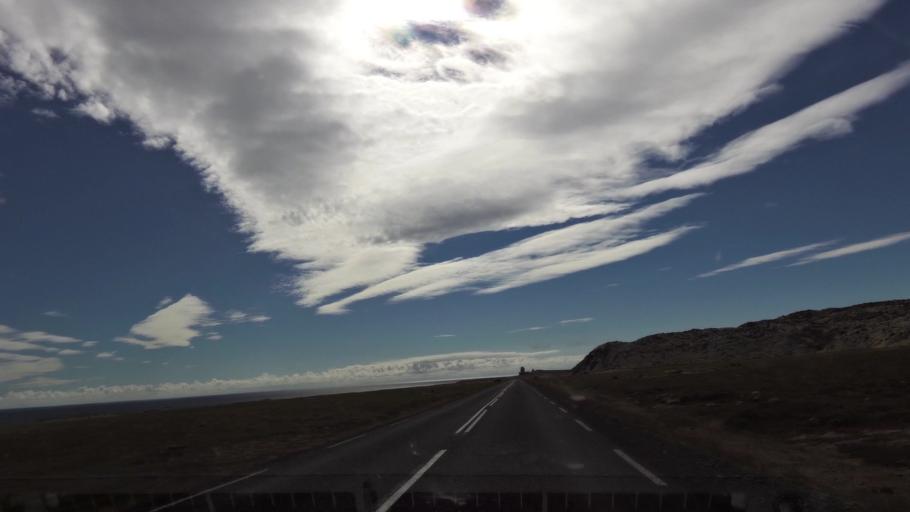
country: IS
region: West
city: Olafsvik
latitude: 64.7466
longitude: -23.7318
